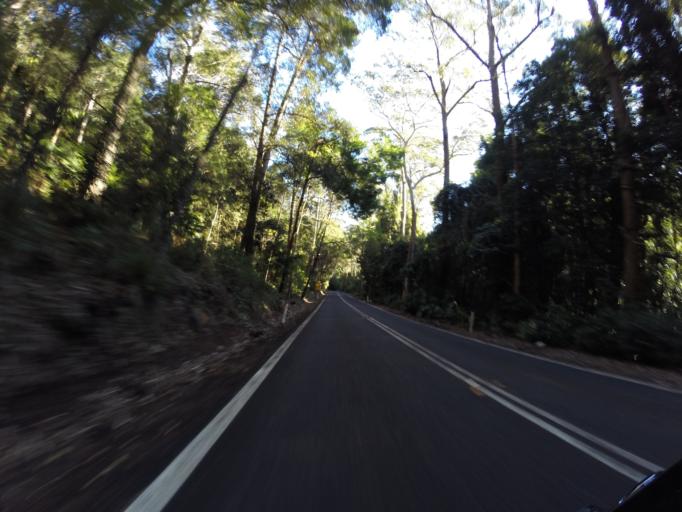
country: AU
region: New South Wales
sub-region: Wollongong
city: Helensburgh
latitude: -34.1827
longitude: 151.0215
